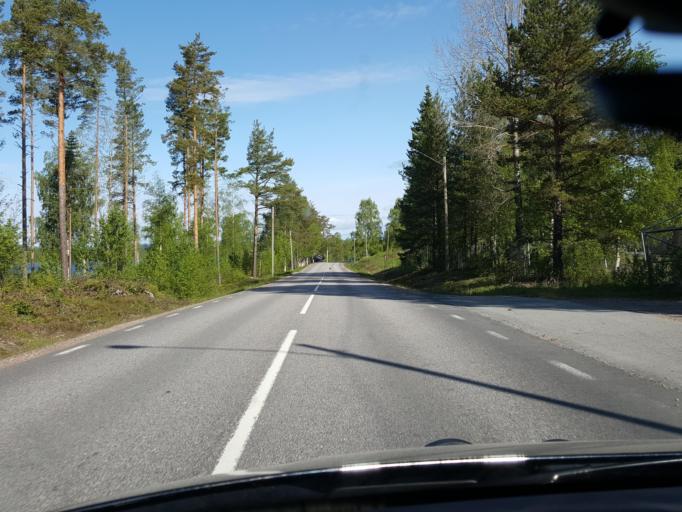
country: SE
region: Vaesternorrland
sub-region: Ange Kommun
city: Ange
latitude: 62.1748
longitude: 15.6625
